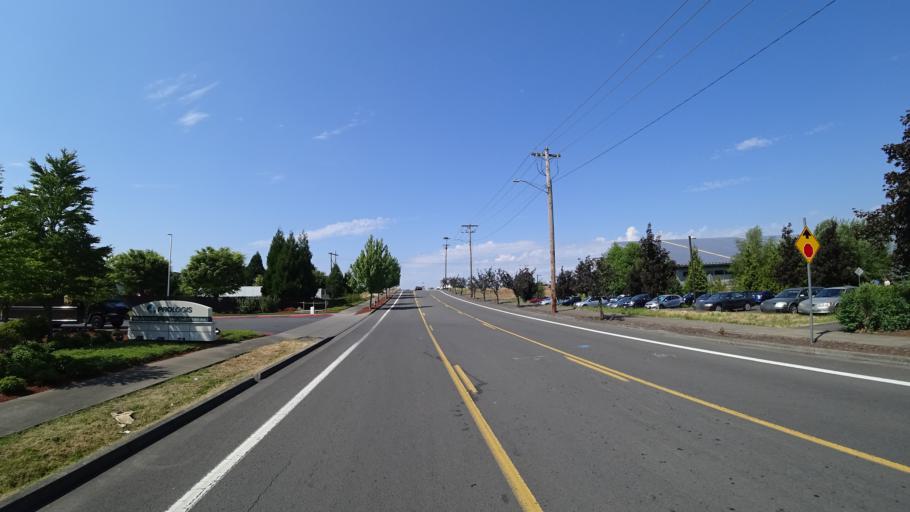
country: US
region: Oregon
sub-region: Multnomah County
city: Fairview
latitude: 45.5620
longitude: -122.5103
